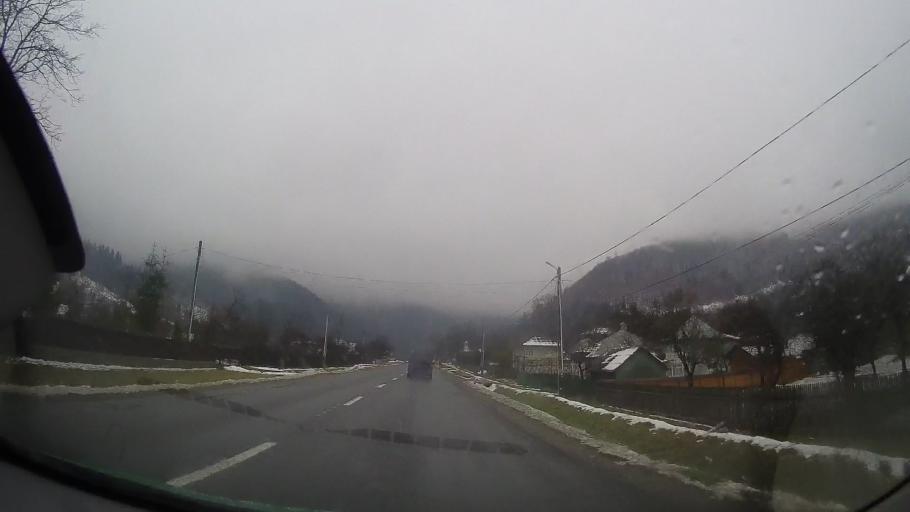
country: RO
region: Neamt
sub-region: Comuna Pangarati
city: Stejaru
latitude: 46.8981
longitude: 26.1714
